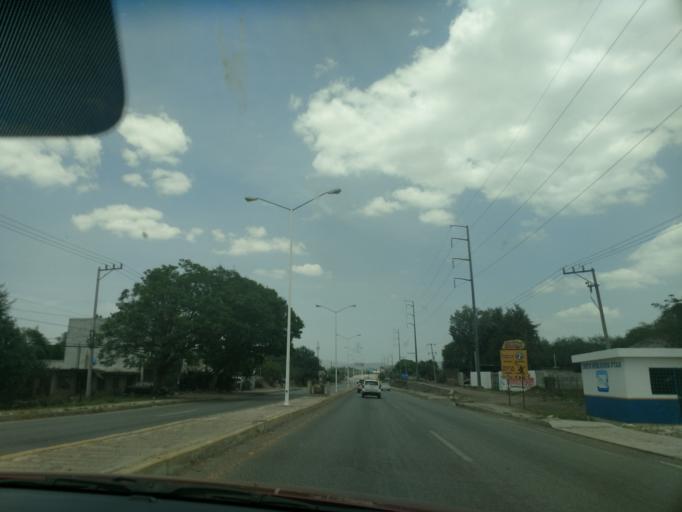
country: MX
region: San Luis Potosi
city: Rio Verde
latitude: 21.9219
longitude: -99.9696
